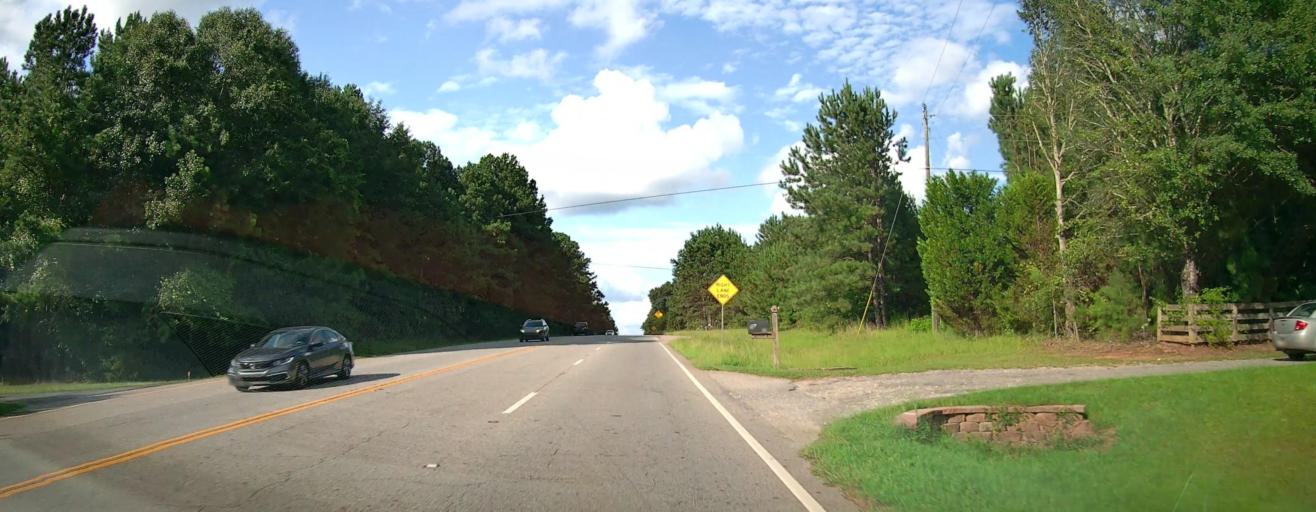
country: US
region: Georgia
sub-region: Coweta County
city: Senoia
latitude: 33.3097
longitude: -84.5303
